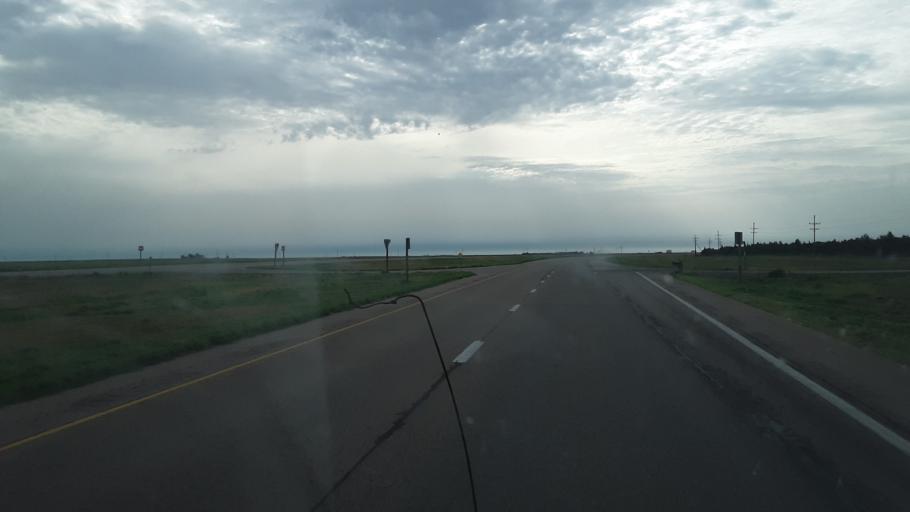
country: US
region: Kansas
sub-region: Finney County
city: Garden City
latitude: 37.9604
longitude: -100.7481
